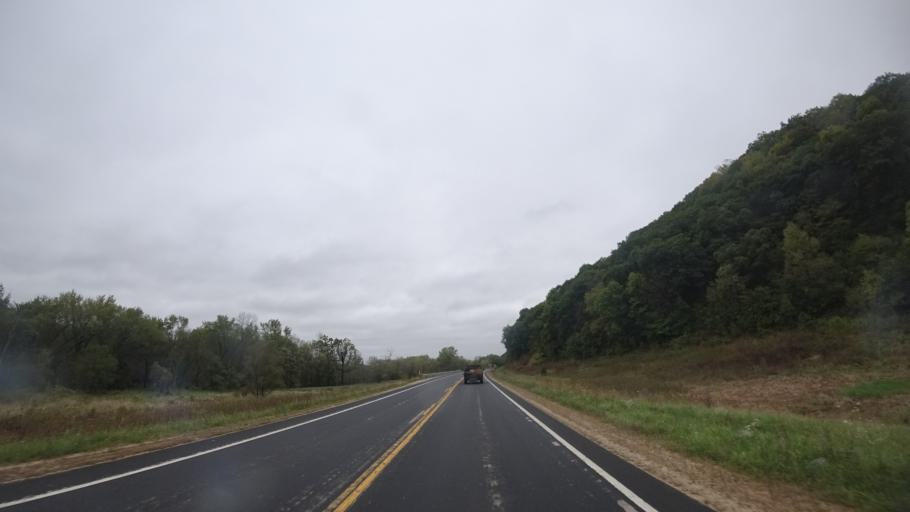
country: US
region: Wisconsin
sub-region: Grant County
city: Boscobel
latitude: 43.1321
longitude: -90.7527
